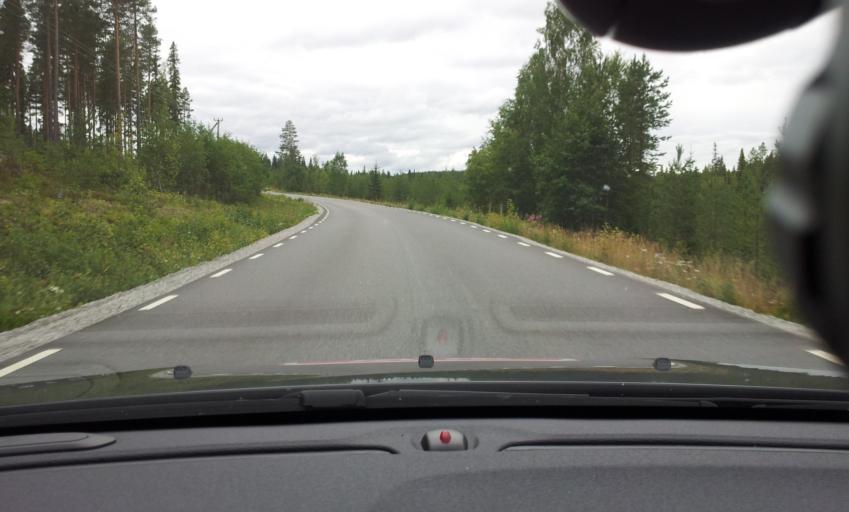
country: SE
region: Jaemtland
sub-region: Braecke Kommun
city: Braecke
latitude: 63.1335
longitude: 15.5106
